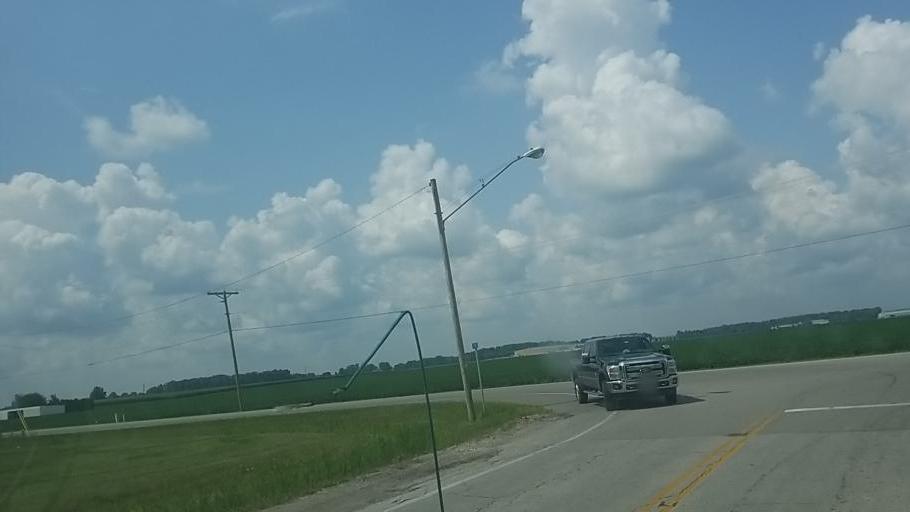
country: US
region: Ohio
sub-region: Wyandot County
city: Upper Sandusky
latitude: 40.8529
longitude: -83.2792
